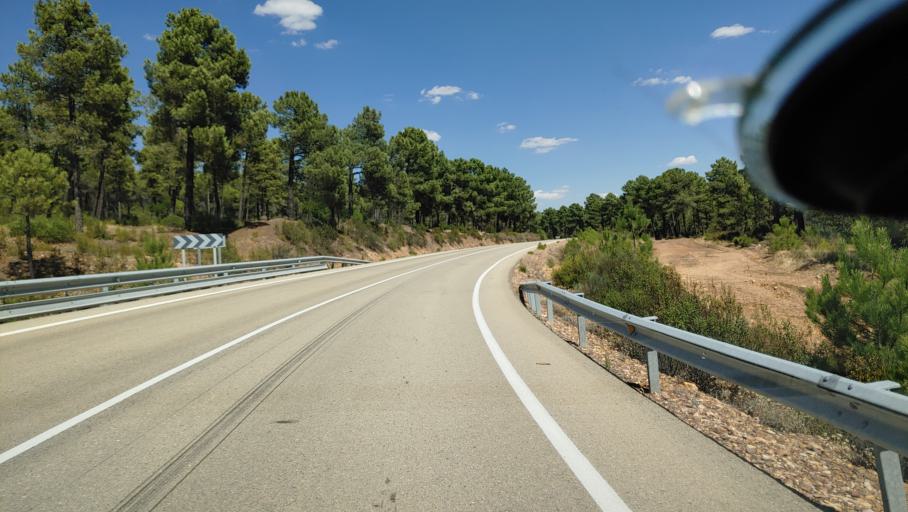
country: ES
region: Castille-La Mancha
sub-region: Provincia de Ciudad Real
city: Saceruela
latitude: 38.9981
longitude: -4.5176
